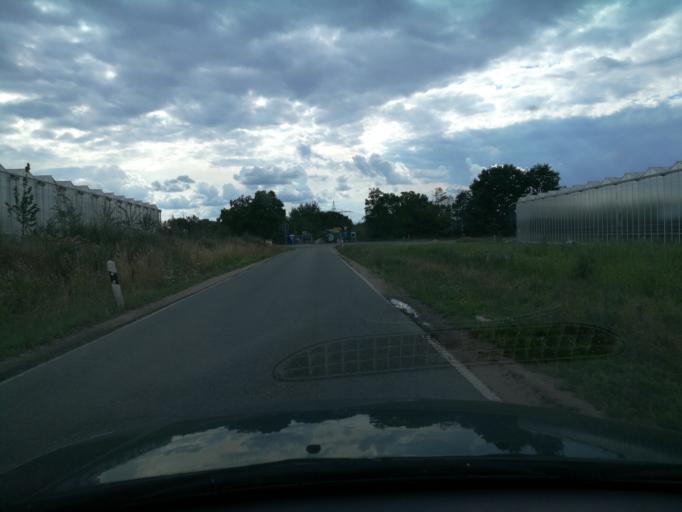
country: DE
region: Bavaria
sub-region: Regierungsbezirk Mittelfranken
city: Wetzendorf
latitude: 49.4821
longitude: 11.0377
